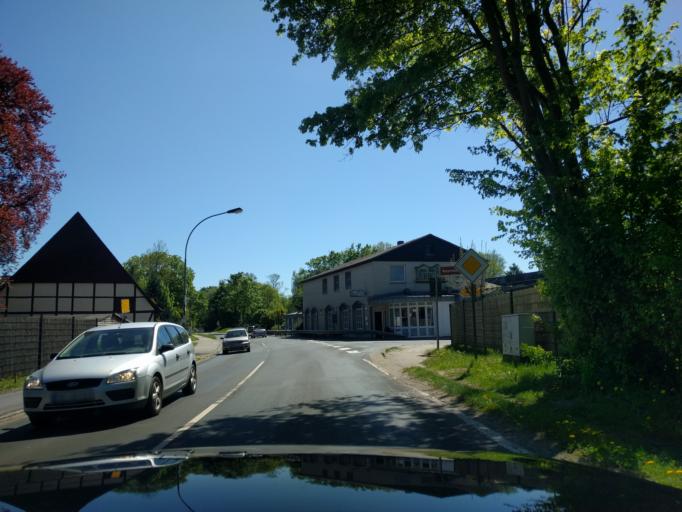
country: DE
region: Lower Saxony
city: Seevetal
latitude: 53.3955
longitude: 10.0116
